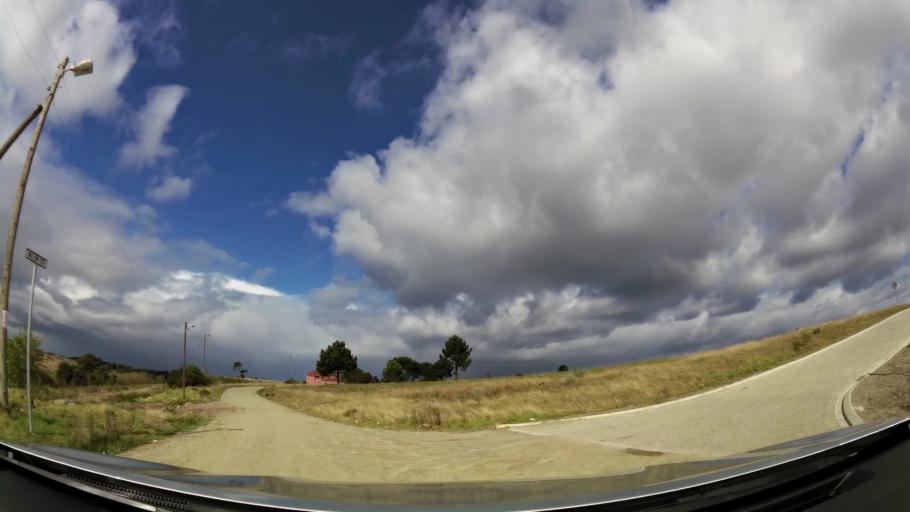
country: ZA
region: Western Cape
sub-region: Eden District Municipality
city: George
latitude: -34.0247
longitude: 22.4683
